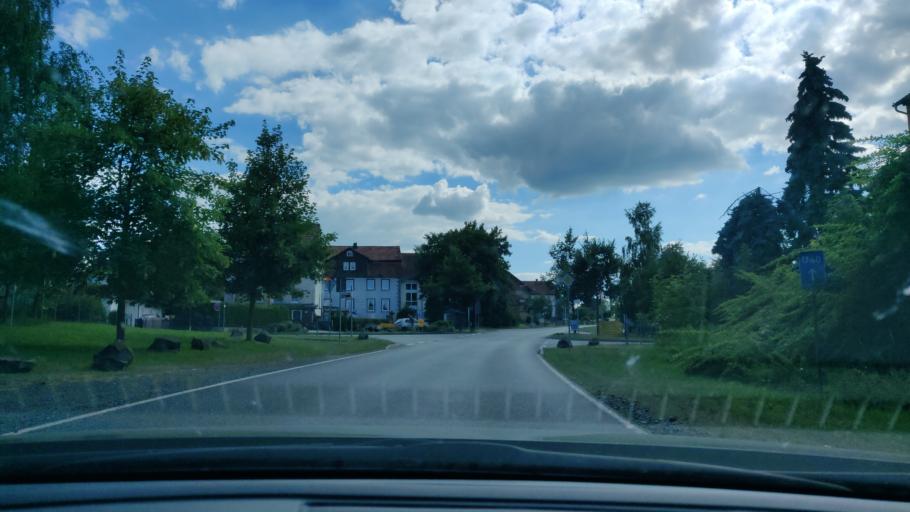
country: DE
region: Hesse
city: Fritzlar
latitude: 51.1570
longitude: 9.3076
